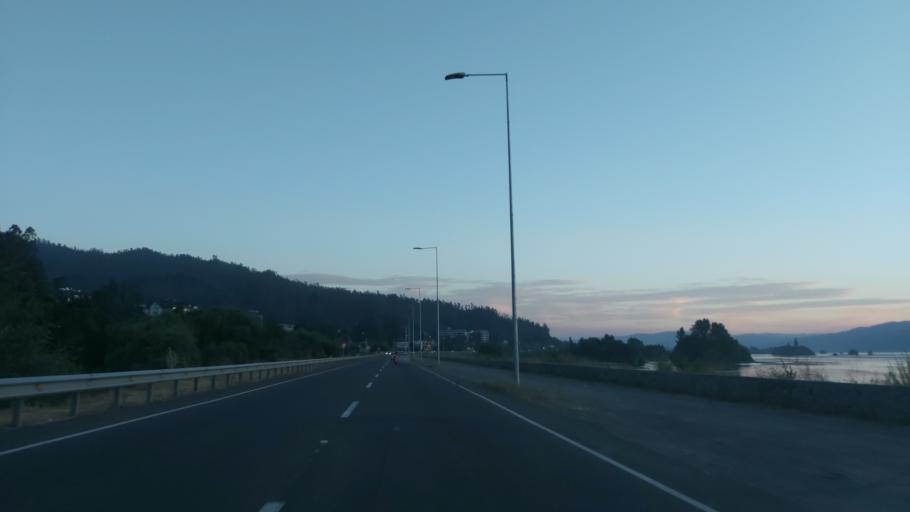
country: CL
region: Biobio
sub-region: Provincia de Concepcion
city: Concepcion
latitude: -36.8753
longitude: -73.0410
